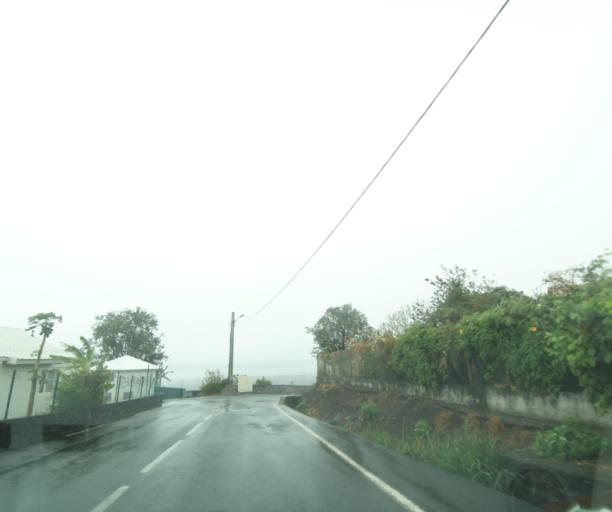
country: RE
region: Reunion
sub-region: Reunion
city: Saint-Paul
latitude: -21.0289
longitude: 55.2852
